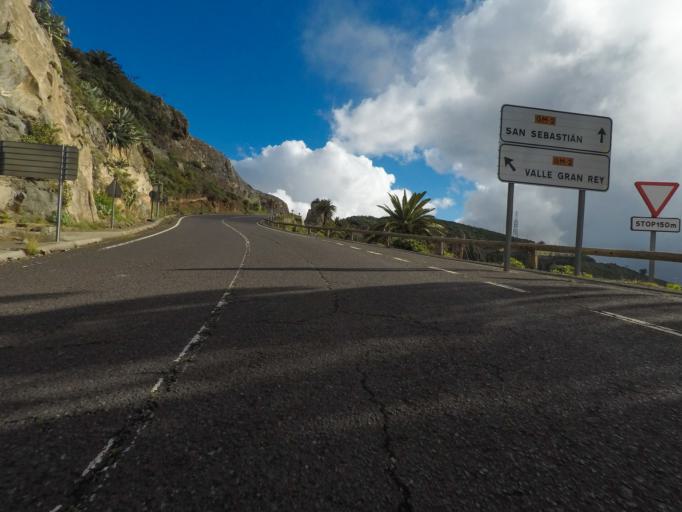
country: ES
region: Canary Islands
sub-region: Provincia de Santa Cruz de Tenerife
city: Alajero
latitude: 28.0987
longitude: -17.1865
